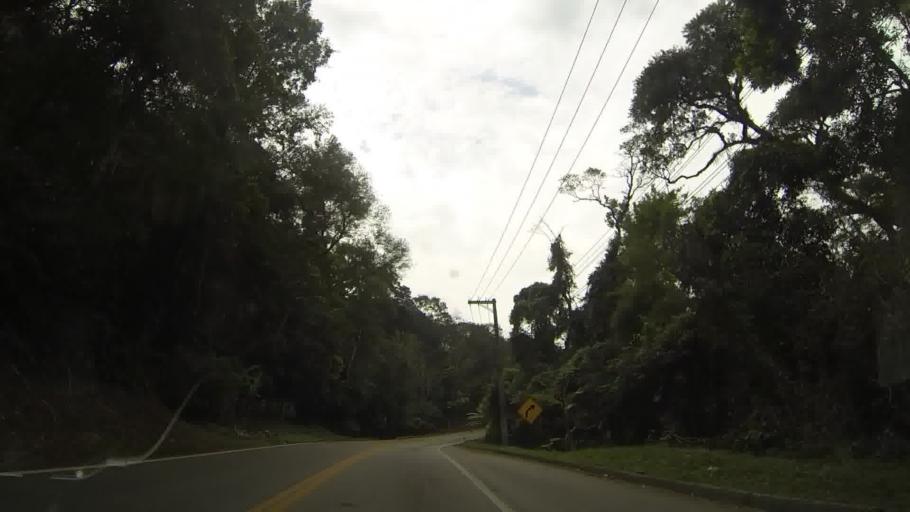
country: BR
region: Sao Paulo
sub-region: Sao Sebastiao
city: Sao Sebastiao
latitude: -23.8304
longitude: -45.4993
